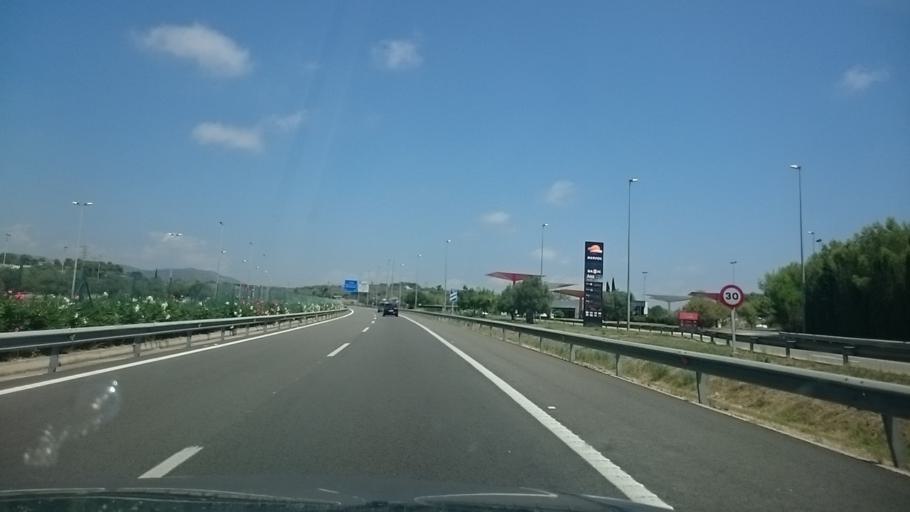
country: ES
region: Catalonia
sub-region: Provincia de Barcelona
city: Cubelles
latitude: 41.2192
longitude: 1.6746
